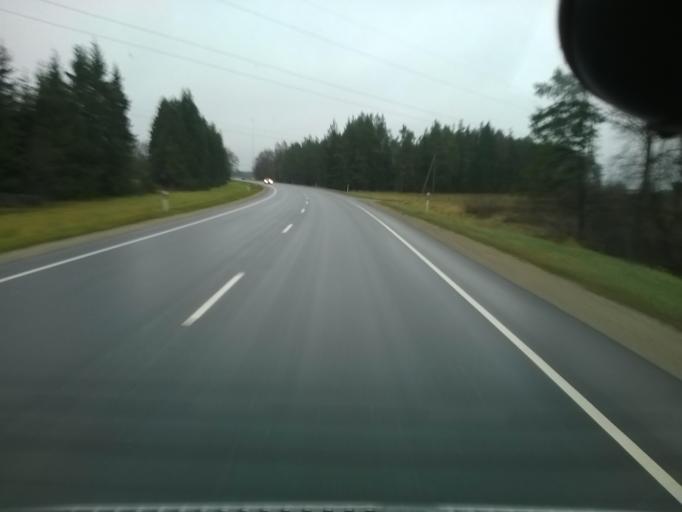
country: EE
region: Harju
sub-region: Nissi vald
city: Turba
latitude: 59.0370
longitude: 24.1666
